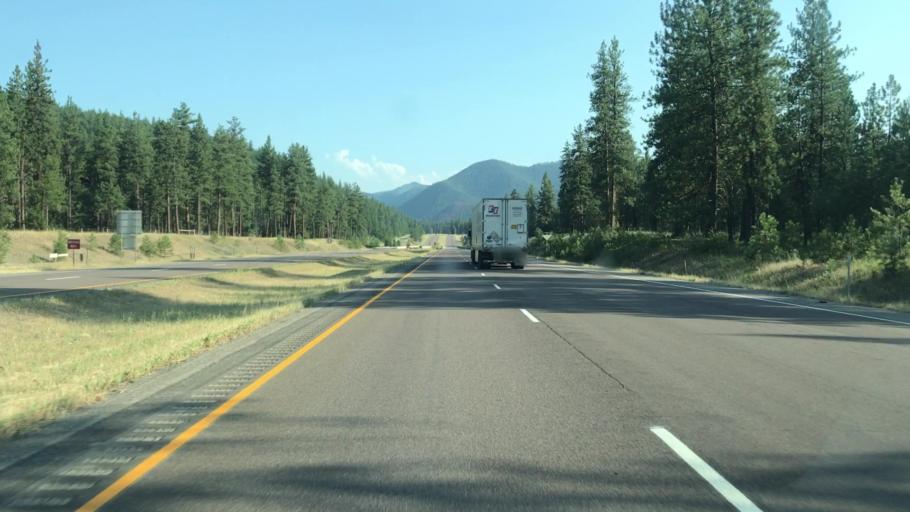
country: US
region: Montana
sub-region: Mineral County
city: Superior
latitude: 47.0728
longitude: -114.7656
